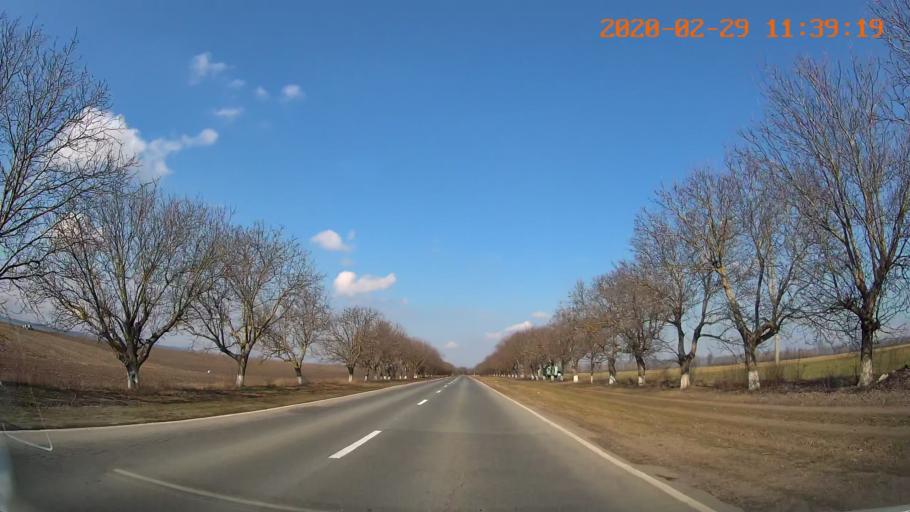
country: MD
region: Rezina
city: Saharna
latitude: 47.6385
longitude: 29.0266
